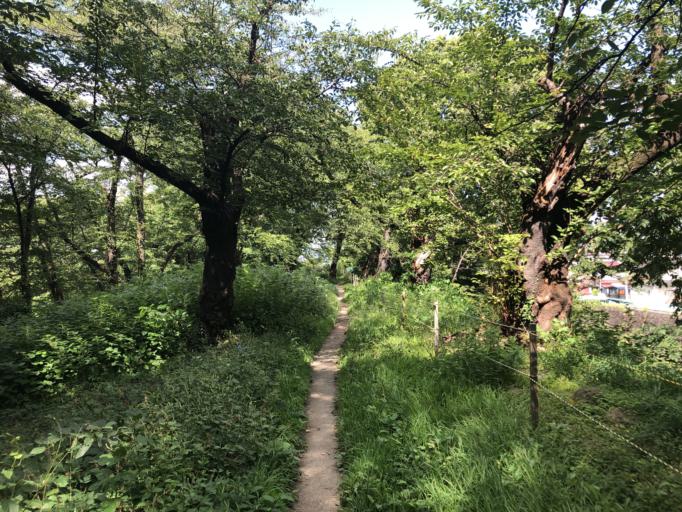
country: JP
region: Yamagata
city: Yamagata-shi
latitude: 38.2561
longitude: 140.3314
